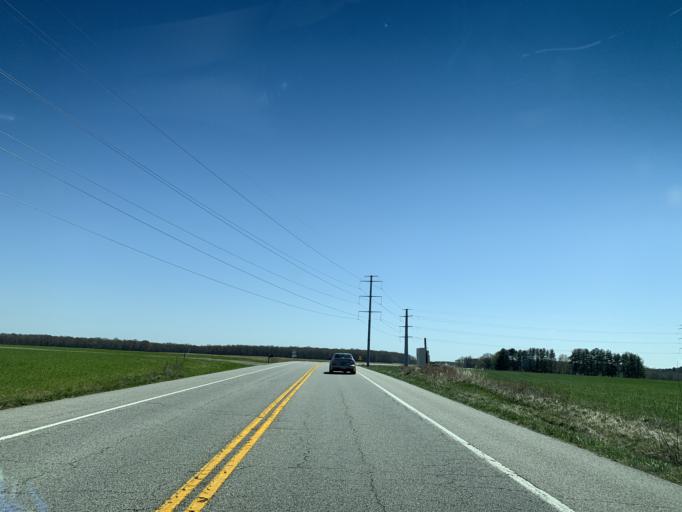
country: US
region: Maryland
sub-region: Queen Anne's County
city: Centreville
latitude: 38.9956
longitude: -76.0457
